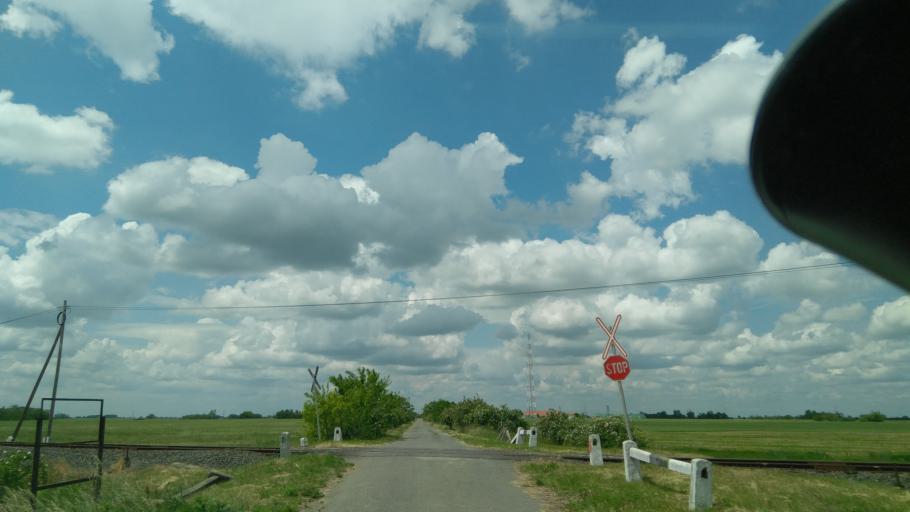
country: HU
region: Bekes
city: Devavanya
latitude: 47.0227
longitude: 20.9370
